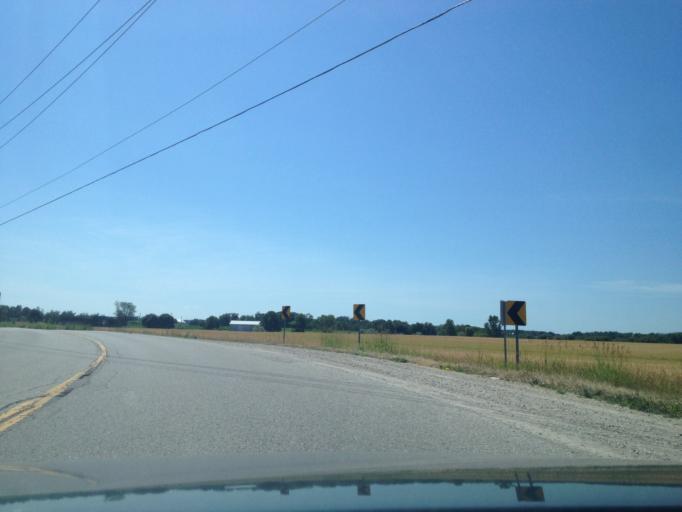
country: CA
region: Ontario
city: Waterloo
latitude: 43.5180
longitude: -80.5180
